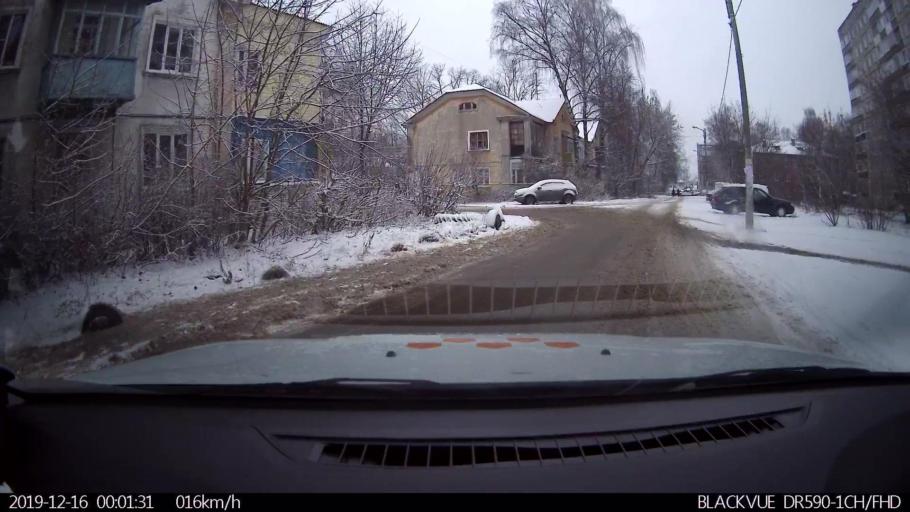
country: RU
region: Nizjnij Novgorod
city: Gorbatovka
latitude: 56.3580
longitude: 43.8446
